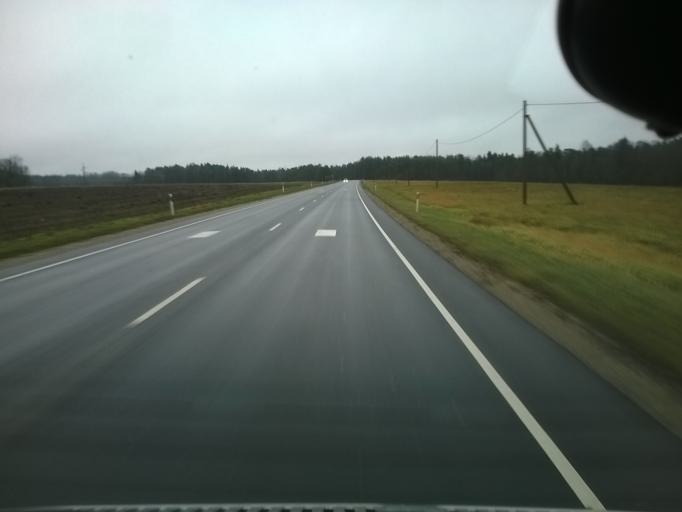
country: EE
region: Harju
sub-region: Nissi vald
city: Turba
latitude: 59.0184
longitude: 24.1418
